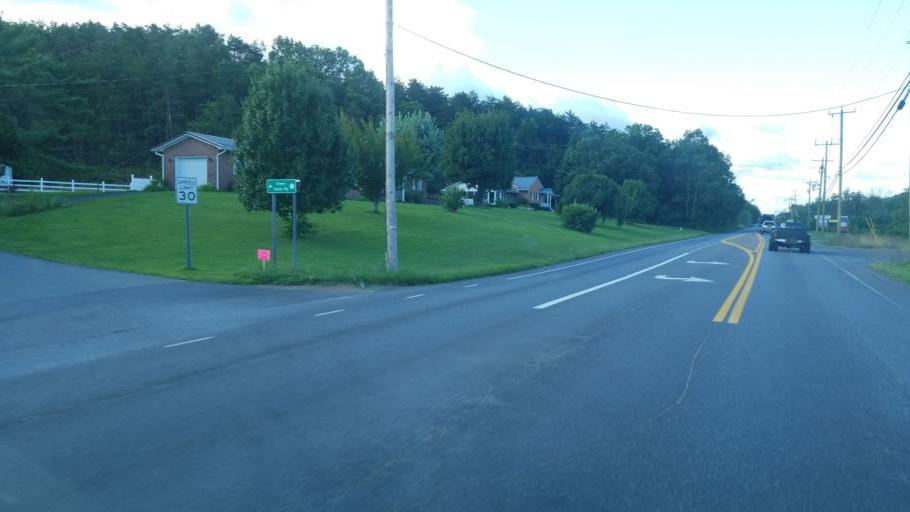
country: US
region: West Virginia
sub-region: Morgan County
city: Berkeley Springs
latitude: 39.5775
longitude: -78.2549
